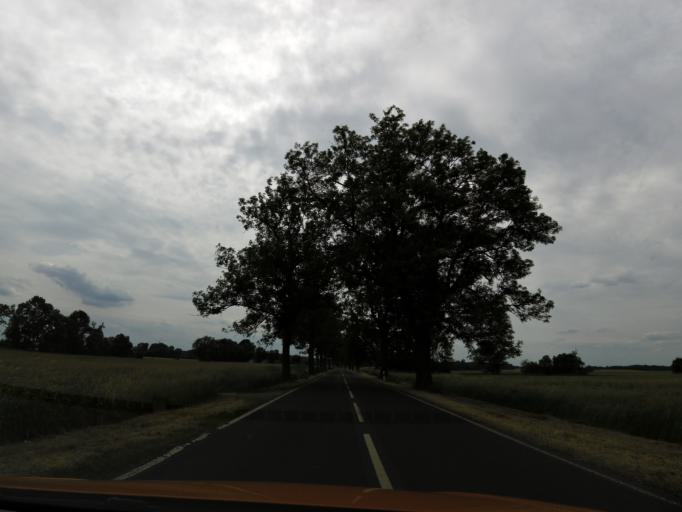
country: DE
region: Brandenburg
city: Rangsdorf
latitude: 52.2884
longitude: 13.3775
